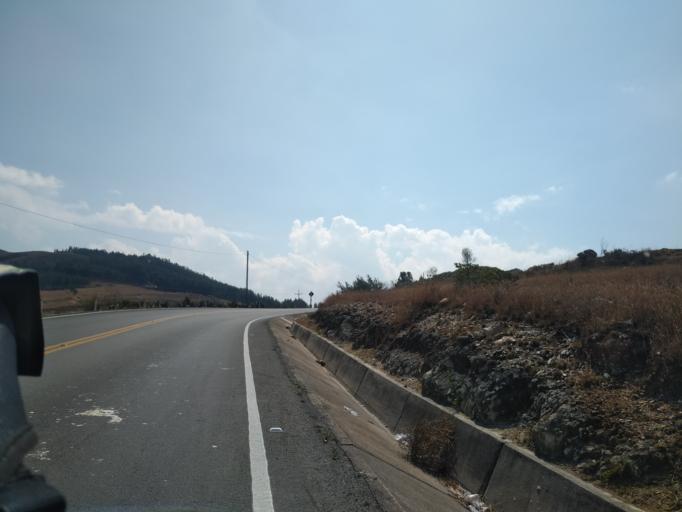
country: PE
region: Cajamarca
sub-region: Provincia de Cajamarca
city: Namora
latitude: -7.2055
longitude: -78.3832
